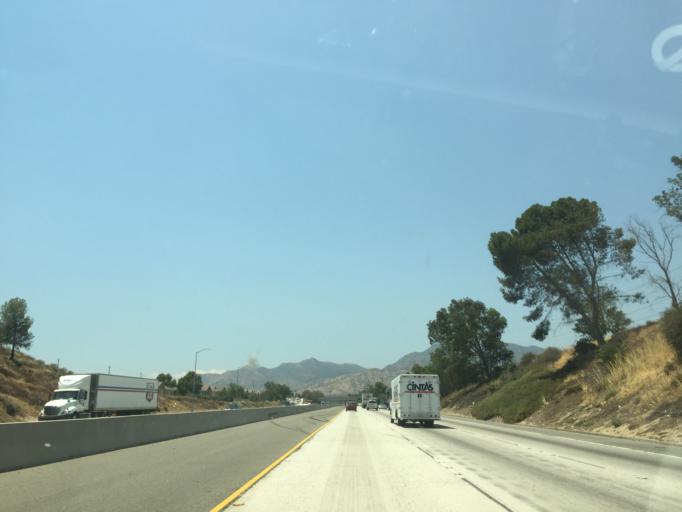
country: US
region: California
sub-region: Los Angeles County
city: San Fernando
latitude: 34.3044
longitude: -118.4249
